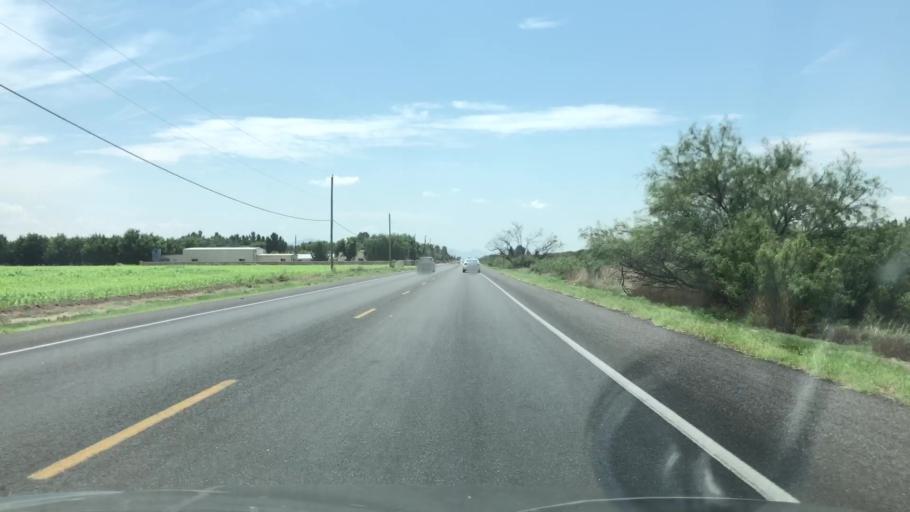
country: US
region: New Mexico
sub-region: Dona Ana County
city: Mesquite
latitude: 32.1847
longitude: -106.7093
